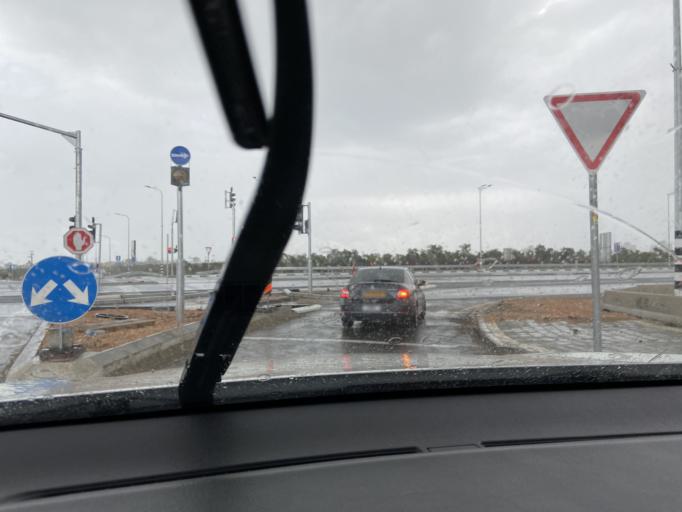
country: IL
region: Northern District
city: El Mazra`a
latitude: 32.9805
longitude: 35.0946
